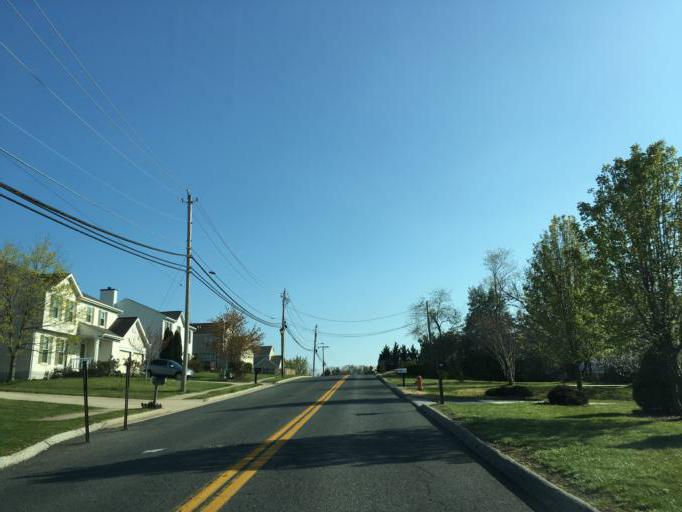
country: US
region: Maryland
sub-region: Baltimore County
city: Carney
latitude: 39.4052
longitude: -76.4962
